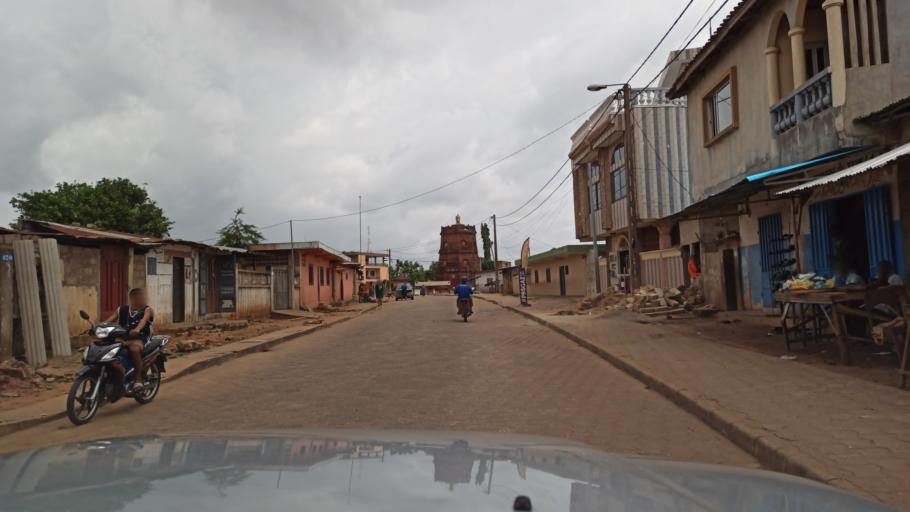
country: BJ
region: Queme
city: Porto-Novo
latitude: 6.4688
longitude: 2.6317
